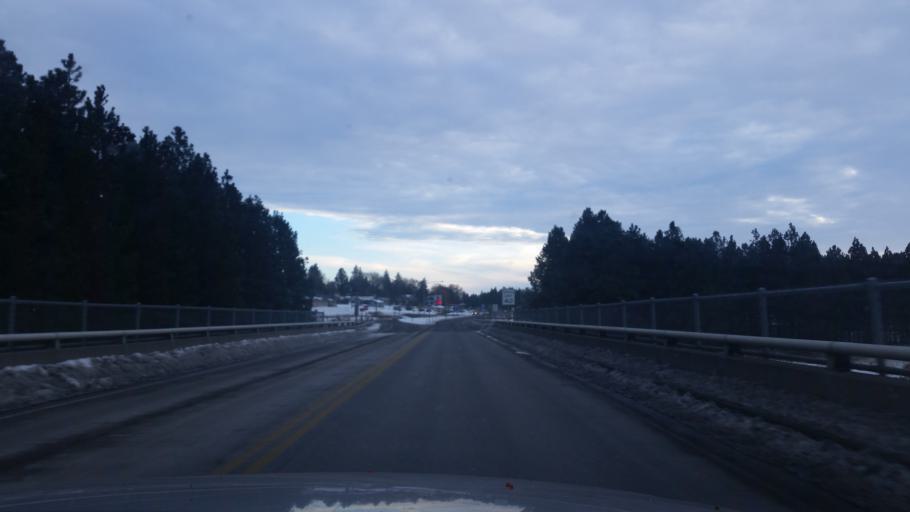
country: US
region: Washington
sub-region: Spokane County
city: Fairchild Air Force Base
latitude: 47.5658
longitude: -117.5939
